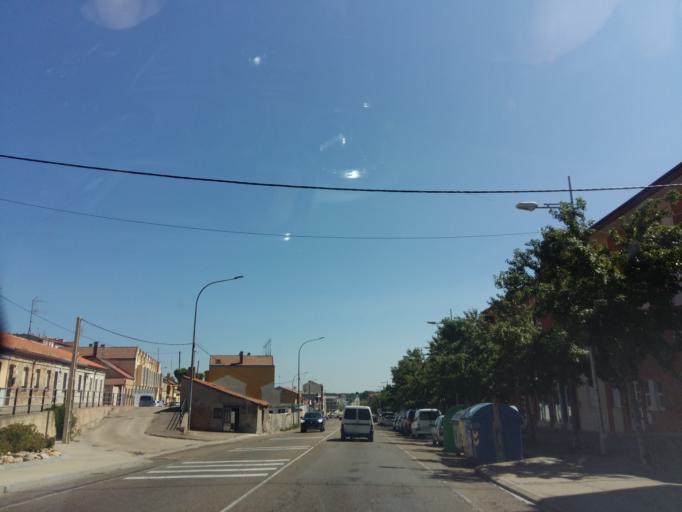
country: ES
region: Castille and Leon
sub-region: Provincia de Leon
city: Astorga
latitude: 42.4552
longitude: -6.0598
